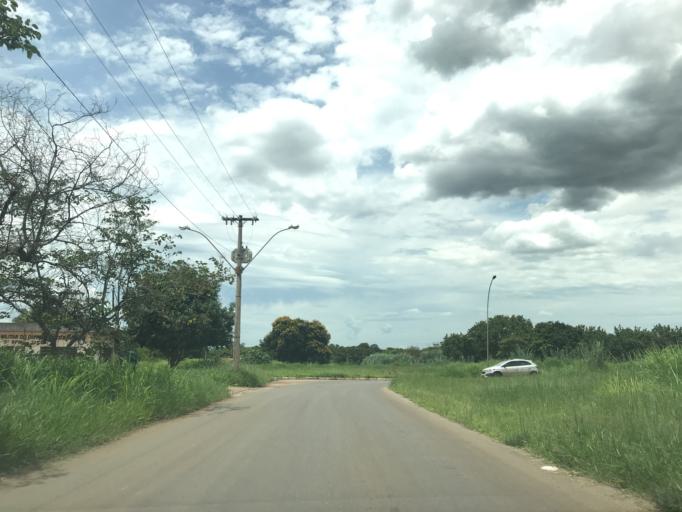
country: BR
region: Federal District
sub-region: Brasilia
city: Brasilia
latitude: -15.8356
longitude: -47.9077
